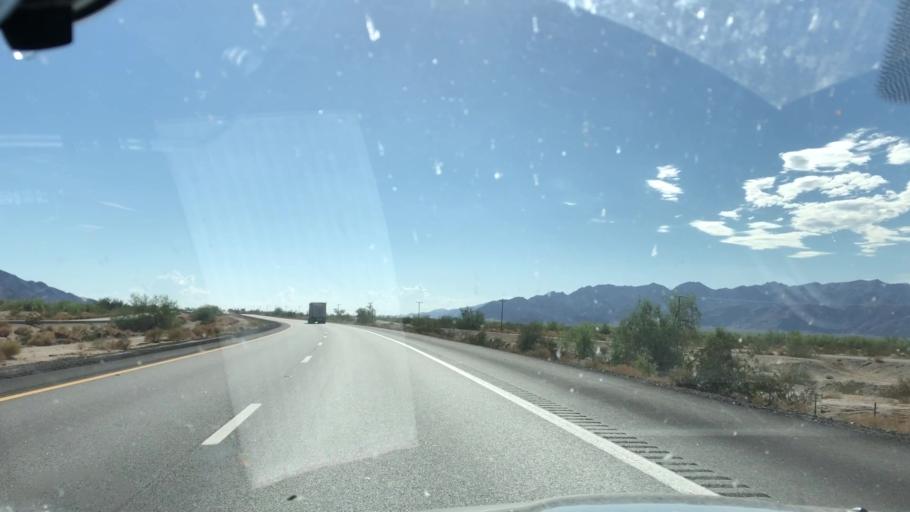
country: US
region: California
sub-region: Imperial County
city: Niland
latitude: 33.7105
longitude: -115.4148
